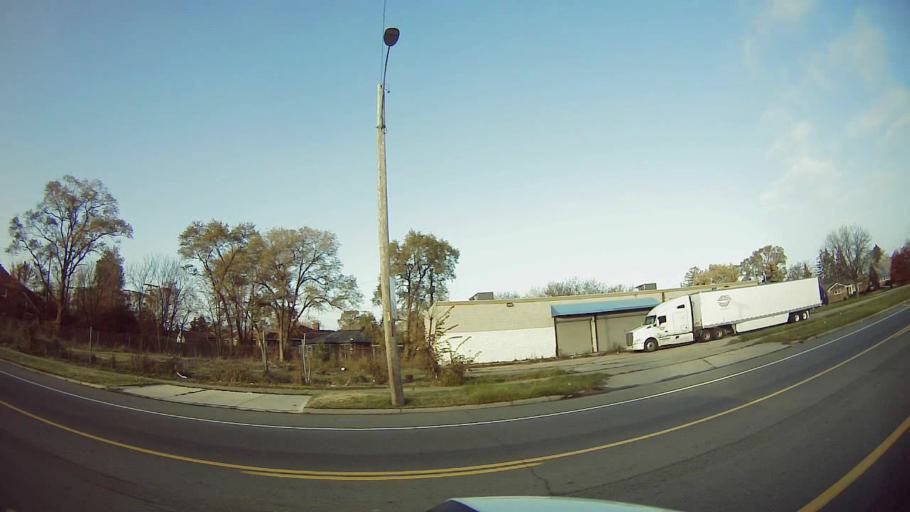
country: US
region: Michigan
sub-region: Wayne County
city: Dearborn
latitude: 42.3608
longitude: -83.1579
